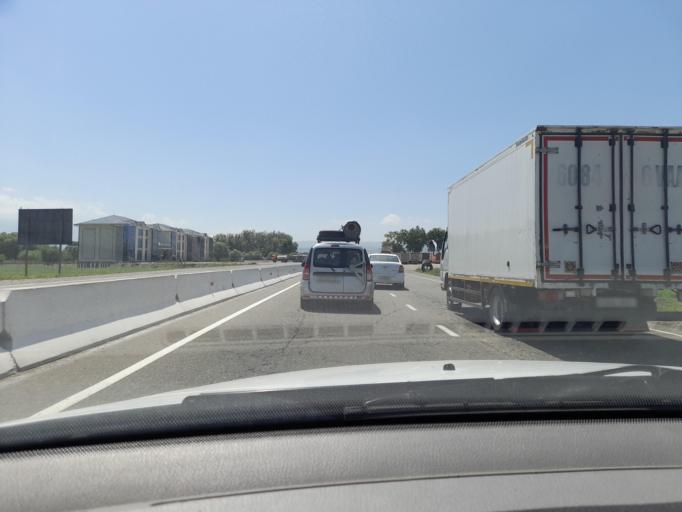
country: UZ
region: Jizzax
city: Jizzax
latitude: 40.0875
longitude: 67.9370
